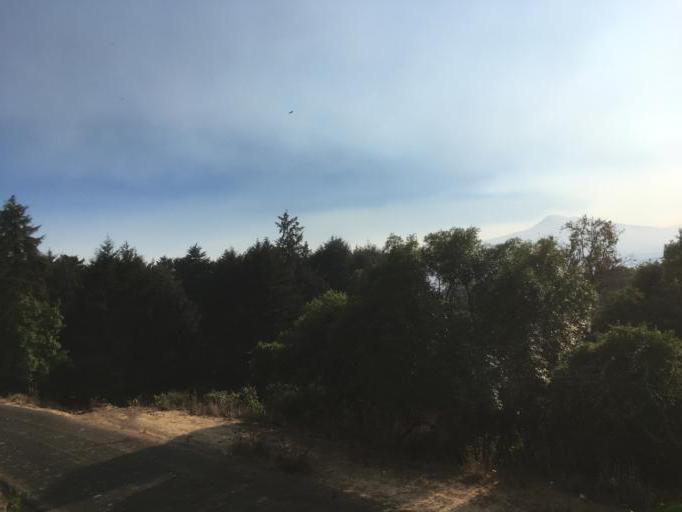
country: MX
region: Michoacan
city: Santa Fe de la Laguna
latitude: 19.6805
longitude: -101.5766
